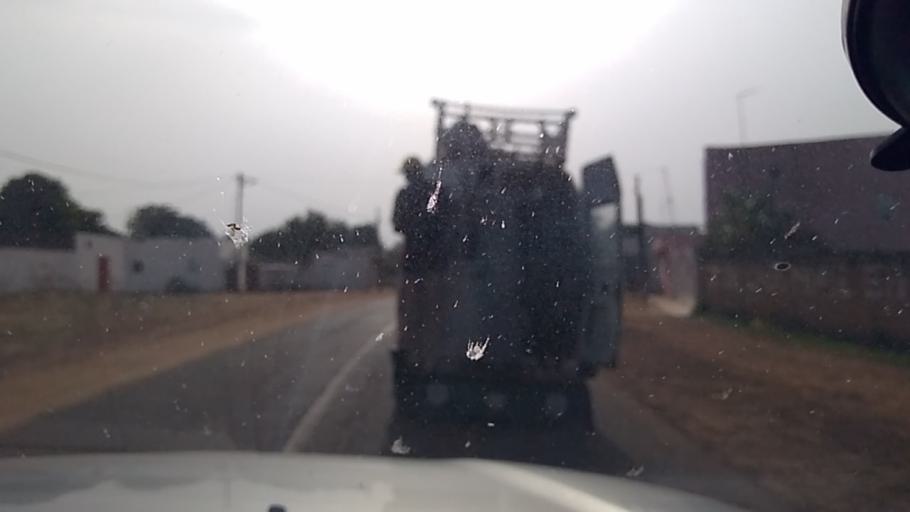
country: SN
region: Thies
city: Mekhe
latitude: 15.1123
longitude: -16.4194
